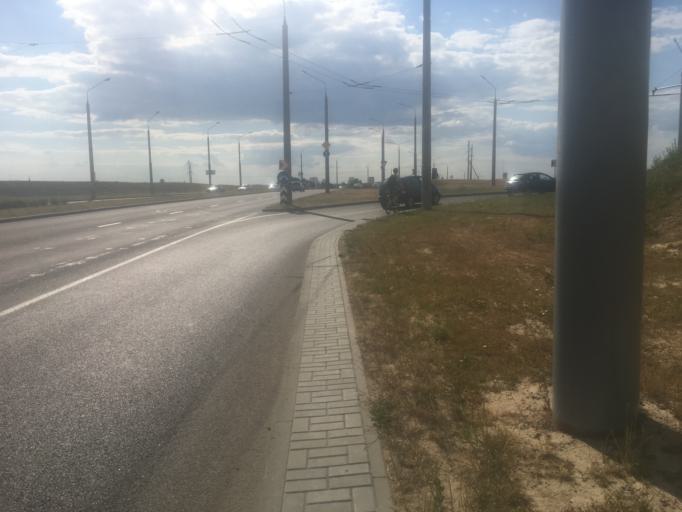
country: BY
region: Grodnenskaya
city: Hrodna
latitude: 53.6461
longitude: 23.8167
